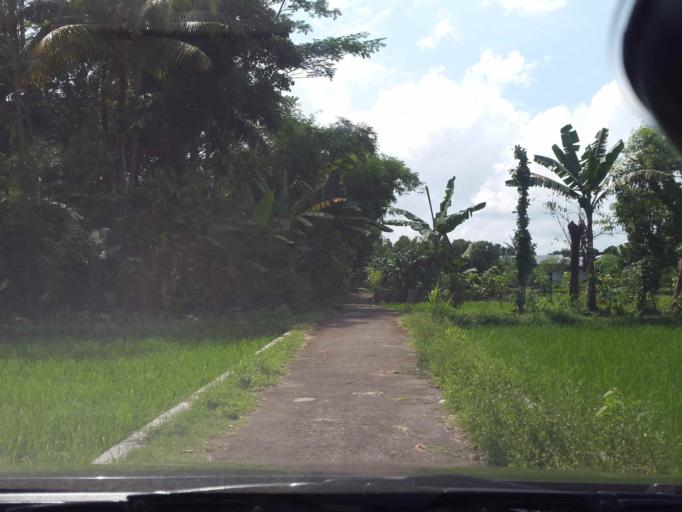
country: ID
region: West Nusa Tenggara
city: Jejelok
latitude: -8.6047
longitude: 116.1690
